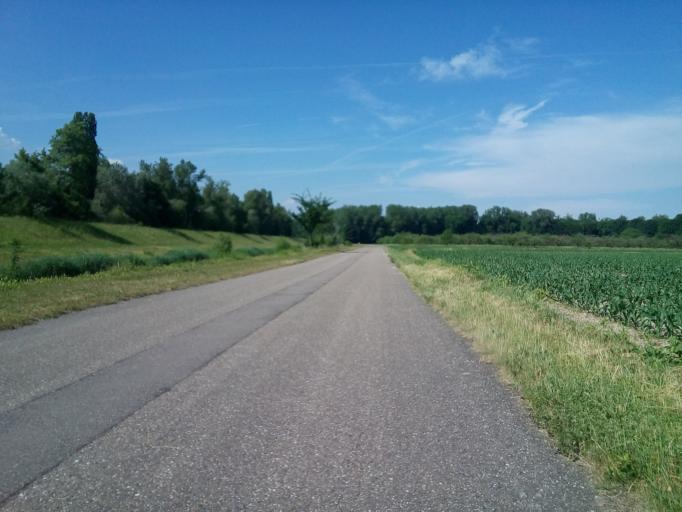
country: DE
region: Baden-Wuerttemberg
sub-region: Karlsruhe Region
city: Lichtenau
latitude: 48.7152
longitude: 7.9663
